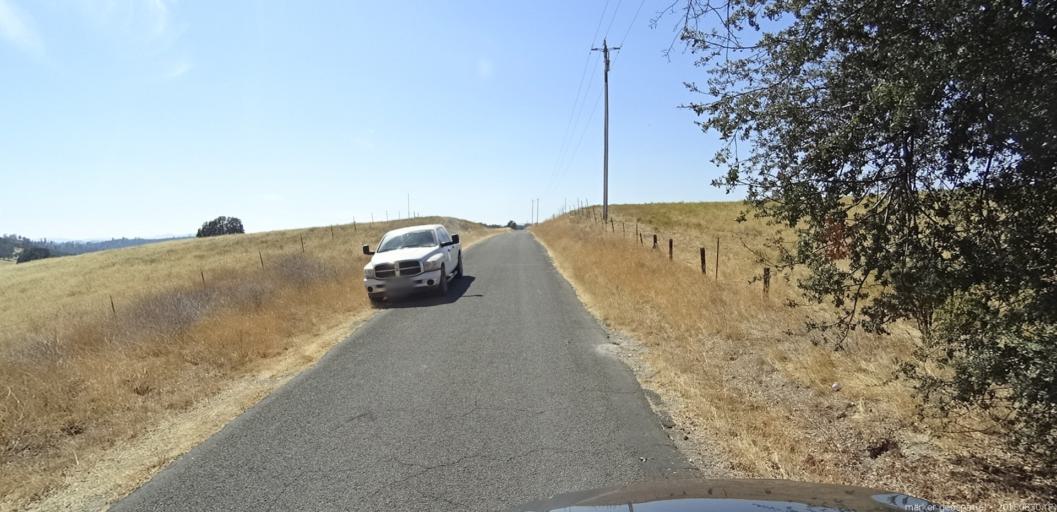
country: US
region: California
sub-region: Monterey County
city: King City
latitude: 36.0099
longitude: -121.1583
